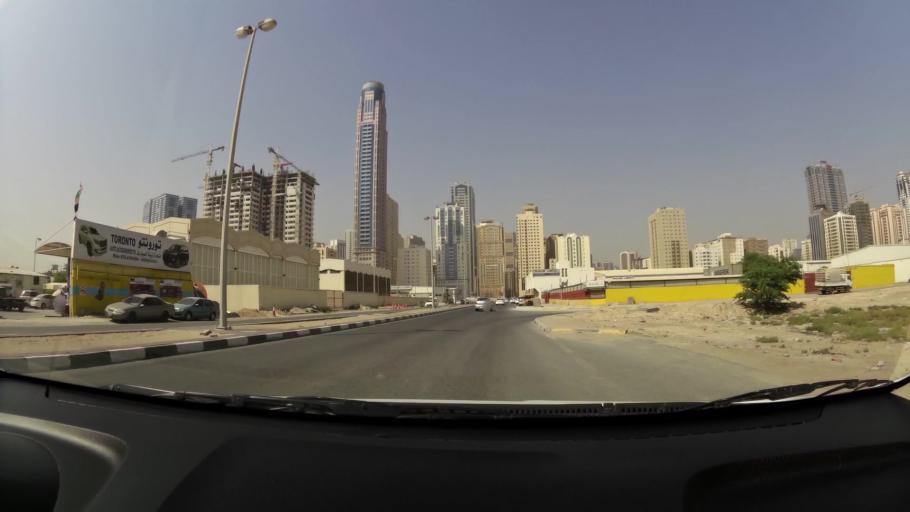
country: AE
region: Ash Shariqah
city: Sharjah
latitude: 25.3087
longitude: 55.3838
